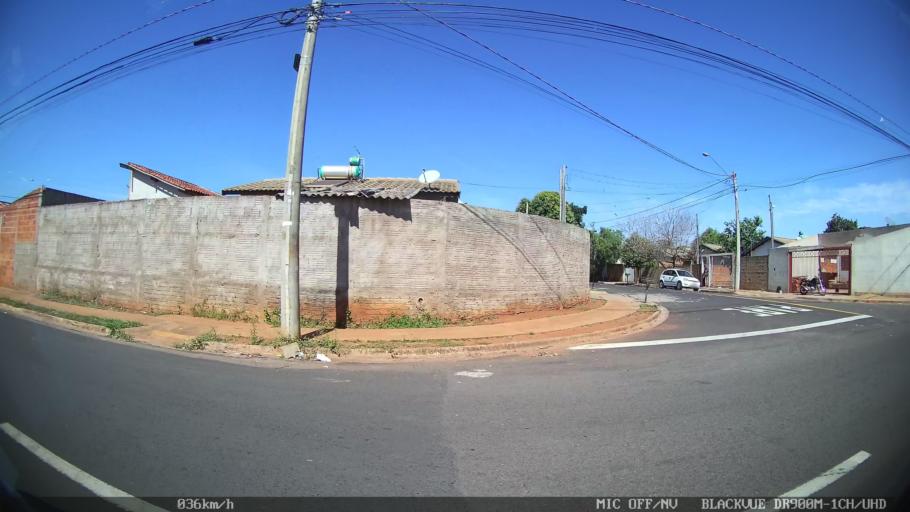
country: BR
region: Sao Paulo
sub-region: Sao Jose Do Rio Preto
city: Sao Jose do Rio Preto
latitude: -20.7405
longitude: -49.4151
